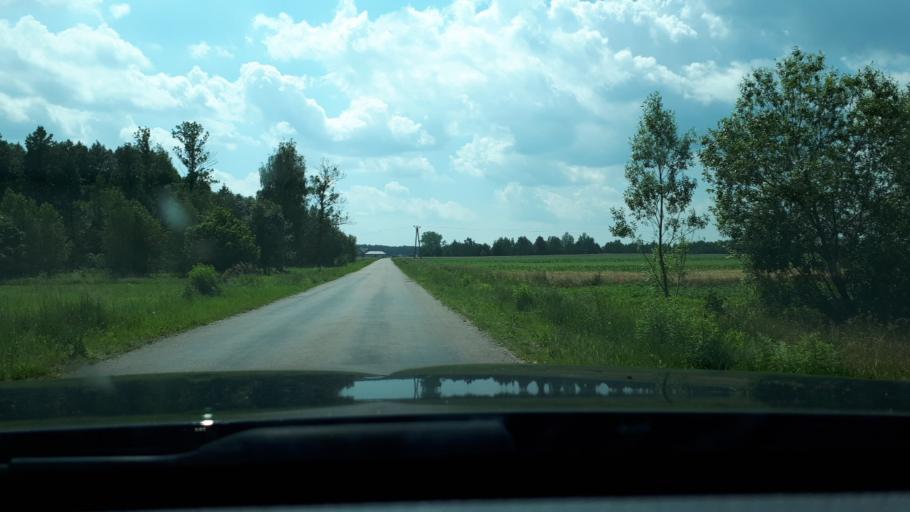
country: PL
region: Podlasie
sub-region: Powiat bialostocki
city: Choroszcz
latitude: 53.1108
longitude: 22.8827
